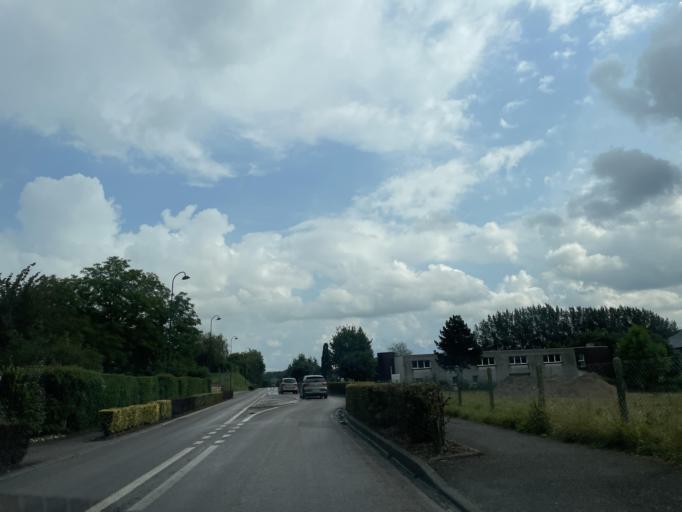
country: FR
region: Haute-Normandie
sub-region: Departement de la Seine-Maritime
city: Envermeu
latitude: 49.8931
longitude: 1.2700
